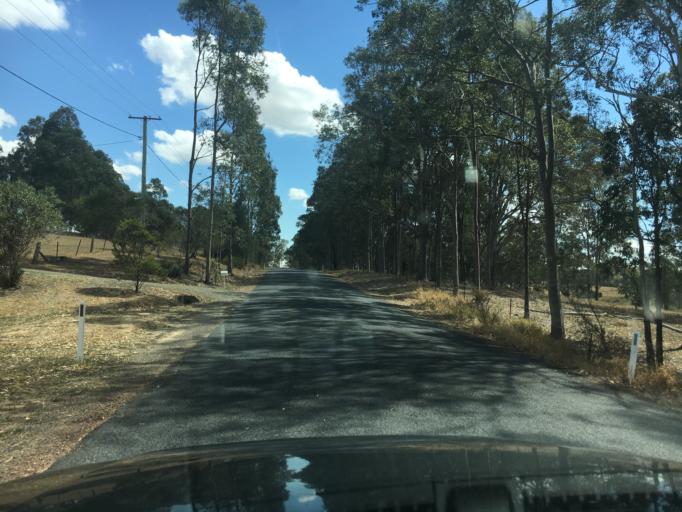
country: AU
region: New South Wales
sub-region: Singleton
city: Singleton
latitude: -32.5150
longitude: 151.1750
